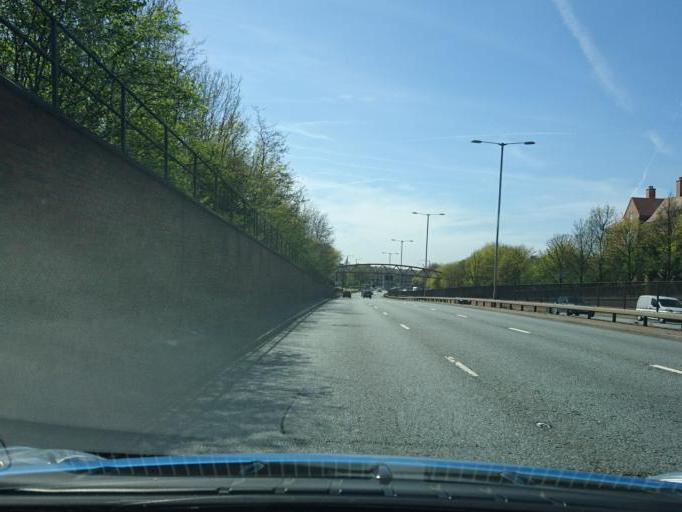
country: GB
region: England
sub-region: Greater London
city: Hendon
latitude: 51.5917
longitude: -0.1893
